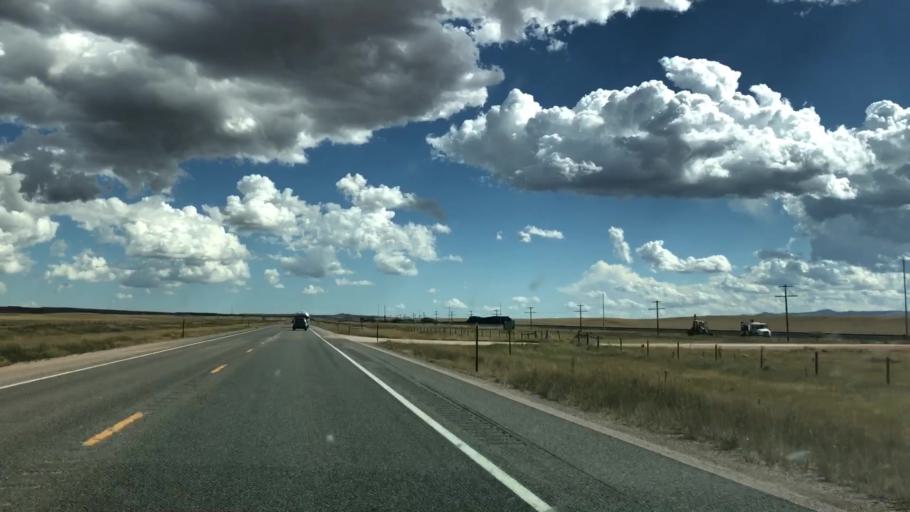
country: US
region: Wyoming
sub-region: Albany County
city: Laramie
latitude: 41.1713
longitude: -105.5868
